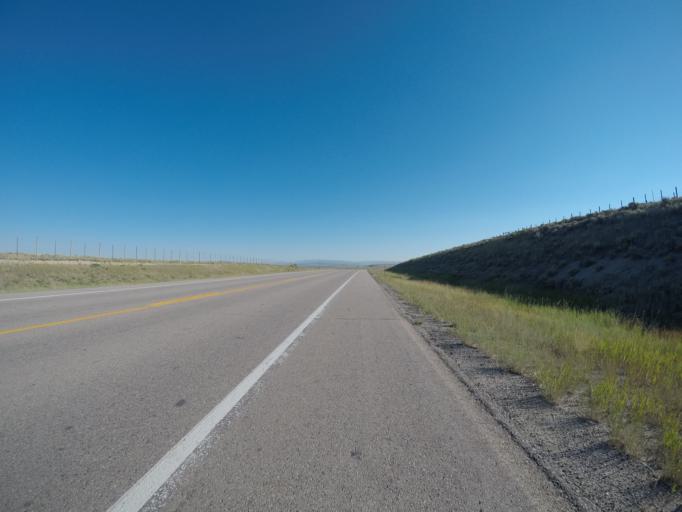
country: US
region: Wyoming
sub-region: Sublette County
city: Pinedale
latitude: 42.9209
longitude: -110.0803
